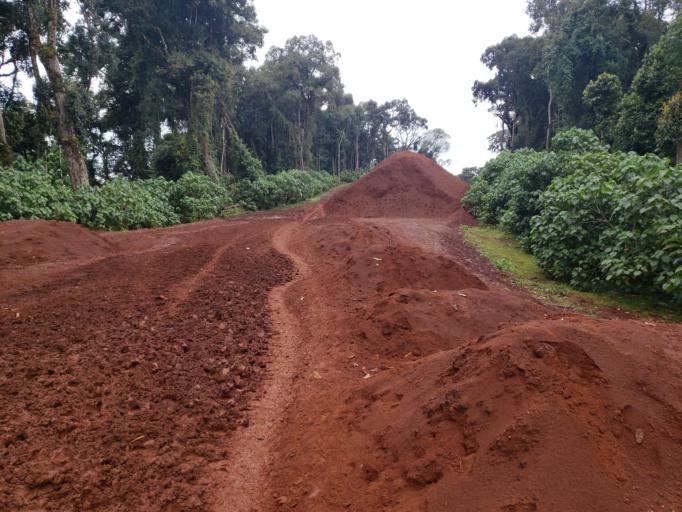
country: ET
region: Oromiya
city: Dodola
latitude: 6.5948
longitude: 39.4126
